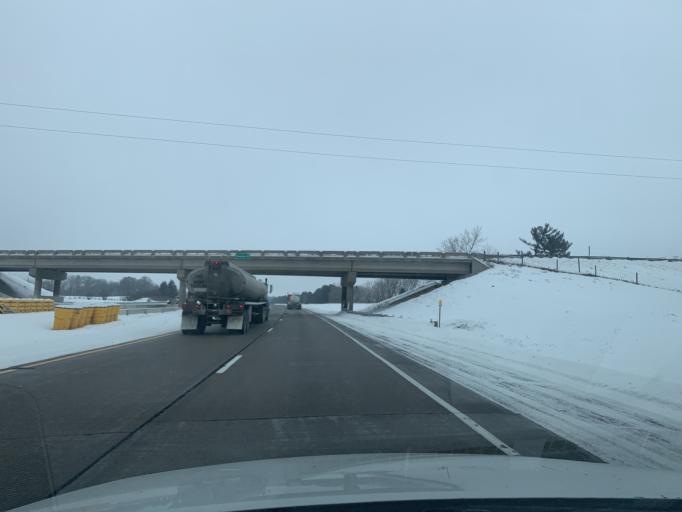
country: US
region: Minnesota
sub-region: Chisago County
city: Harris
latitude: 45.6148
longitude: -92.9923
